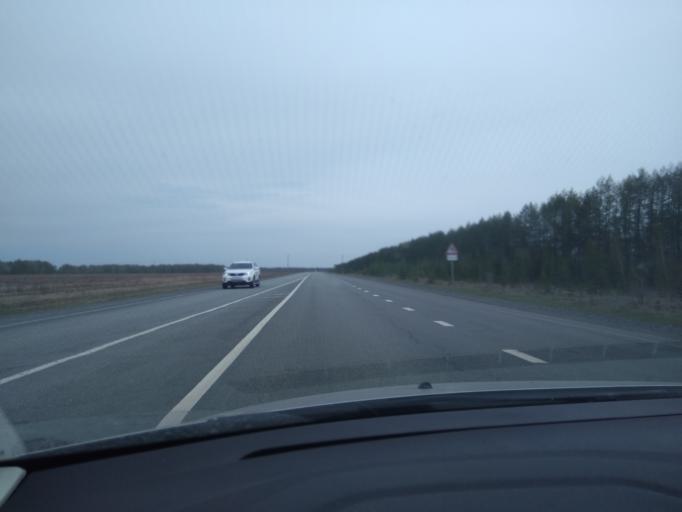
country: RU
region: Sverdlovsk
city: Troitskiy
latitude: 57.0890
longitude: 63.7655
